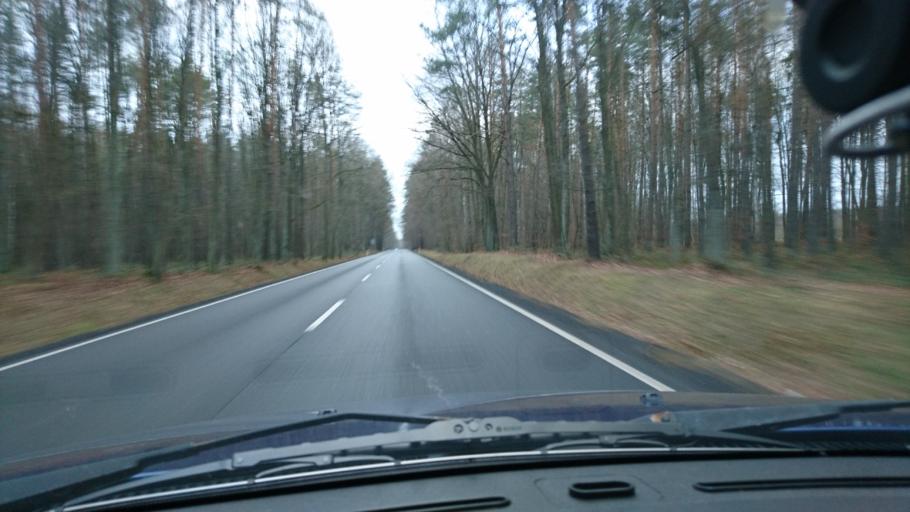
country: PL
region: Opole Voivodeship
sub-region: Powiat oleski
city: Olesno
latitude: 50.9253
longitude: 18.3368
